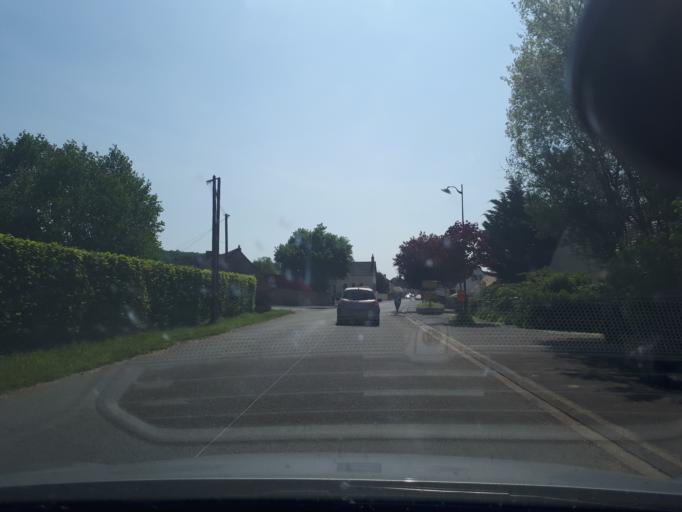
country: FR
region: Pays de la Loire
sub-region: Departement de la Sarthe
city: Le Breil-sur-Merize
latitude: 48.0114
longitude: 0.4735
